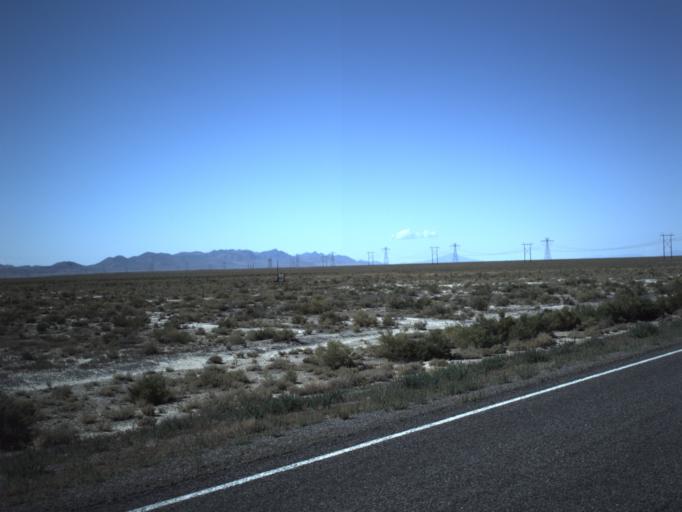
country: US
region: Utah
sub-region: Millard County
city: Delta
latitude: 39.2501
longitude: -112.8979
